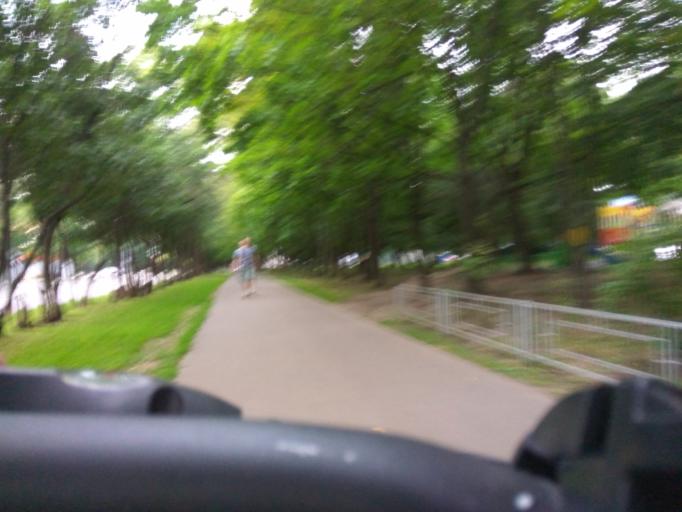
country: RU
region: Moscow
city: Tsaritsyno
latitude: 55.6233
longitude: 37.6561
